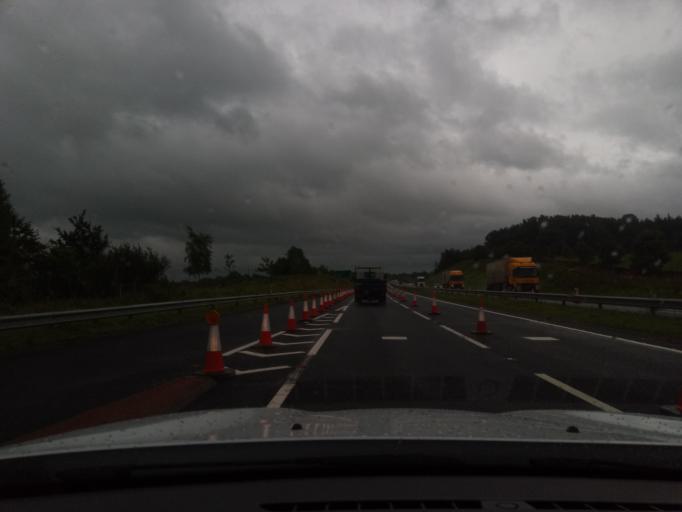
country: GB
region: England
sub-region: Cumbria
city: Penrith
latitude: 54.6436
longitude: -2.6179
